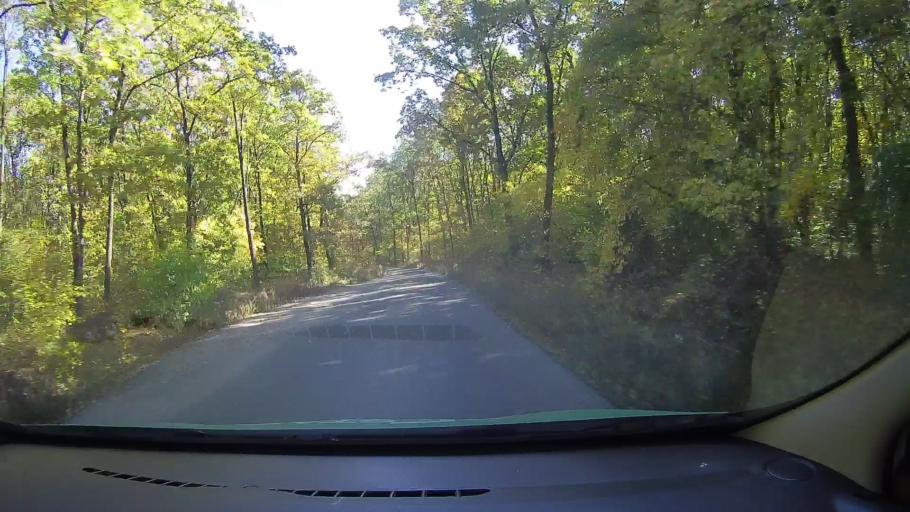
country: RO
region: Satu Mare
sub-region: Comuna Terebesti
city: Terebesti
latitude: 47.7081
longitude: 22.7560
